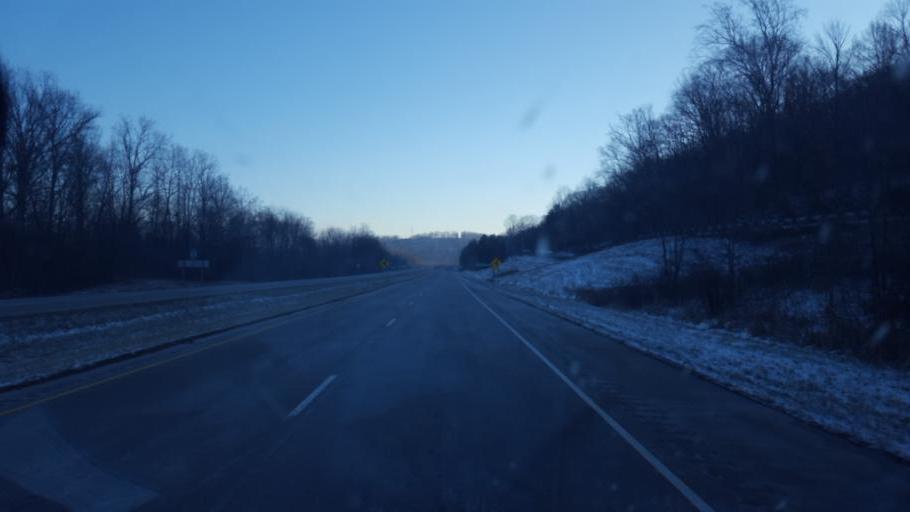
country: US
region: Ohio
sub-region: Pike County
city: Piketon
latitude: 39.0453
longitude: -83.1431
